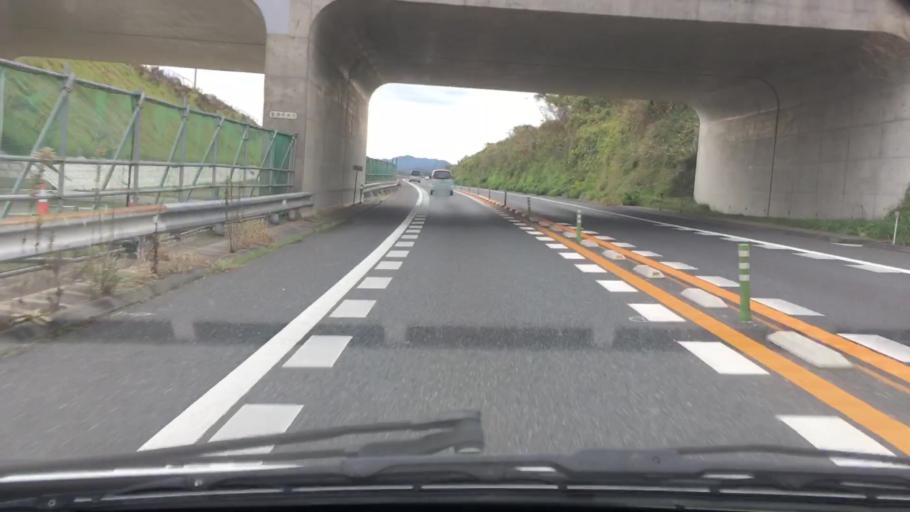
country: JP
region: Chiba
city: Kimitsu
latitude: 35.2410
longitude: 139.8885
